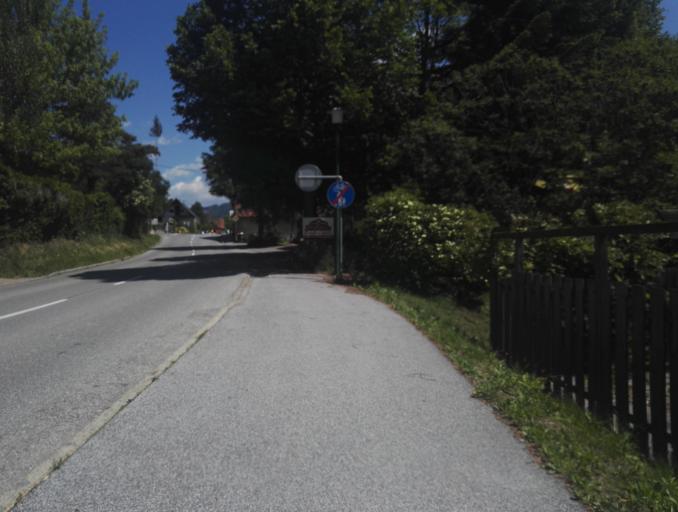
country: AT
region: Styria
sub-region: Politischer Bezirk Graz-Umgebung
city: Deutschfeistritz
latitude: 47.1772
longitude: 15.3210
